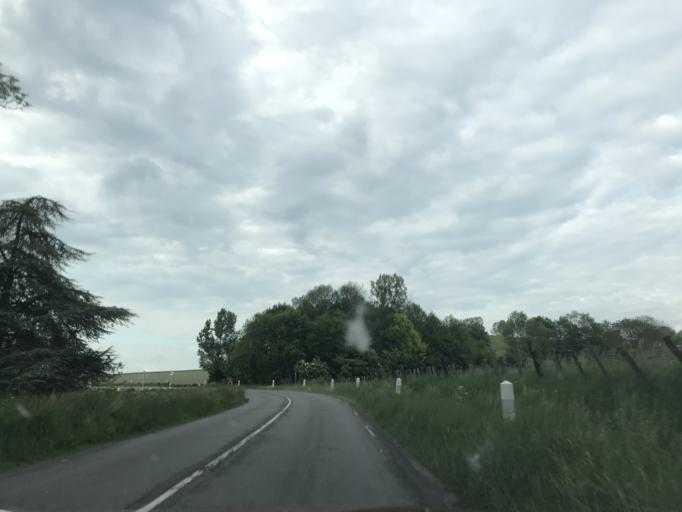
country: FR
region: Auvergne
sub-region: Departement du Puy-de-Dome
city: Maringues
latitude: 45.9524
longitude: 3.3251
